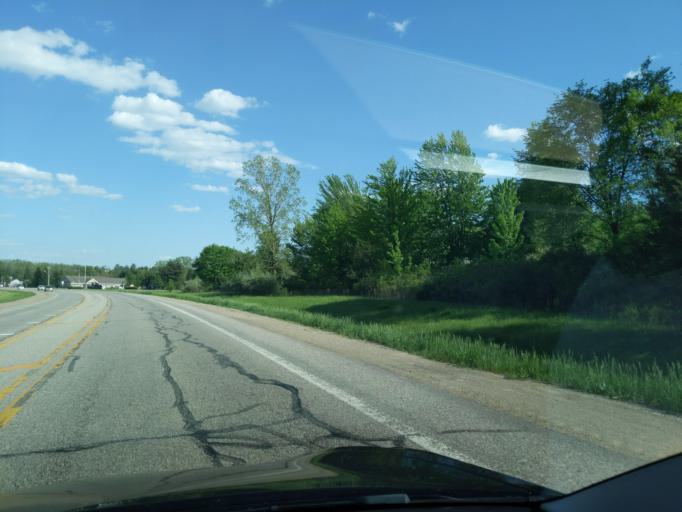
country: US
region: Michigan
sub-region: Eaton County
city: Grand Ledge
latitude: 42.7425
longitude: -84.7577
